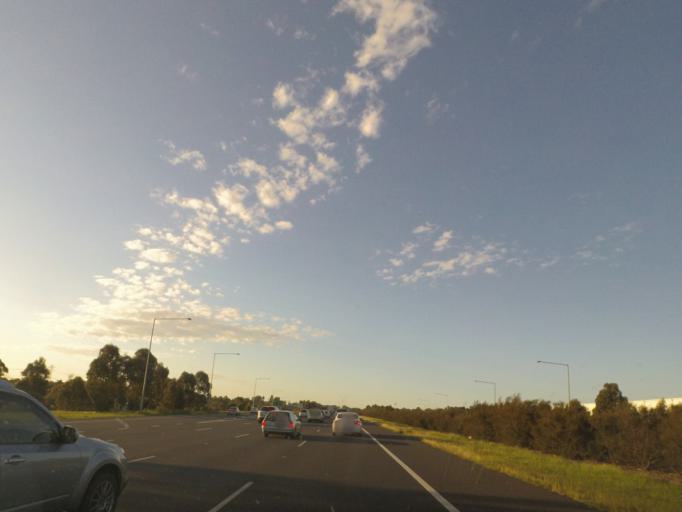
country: AU
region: Victoria
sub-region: Monash
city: Mulgrave
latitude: -37.9074
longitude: 145.2158
